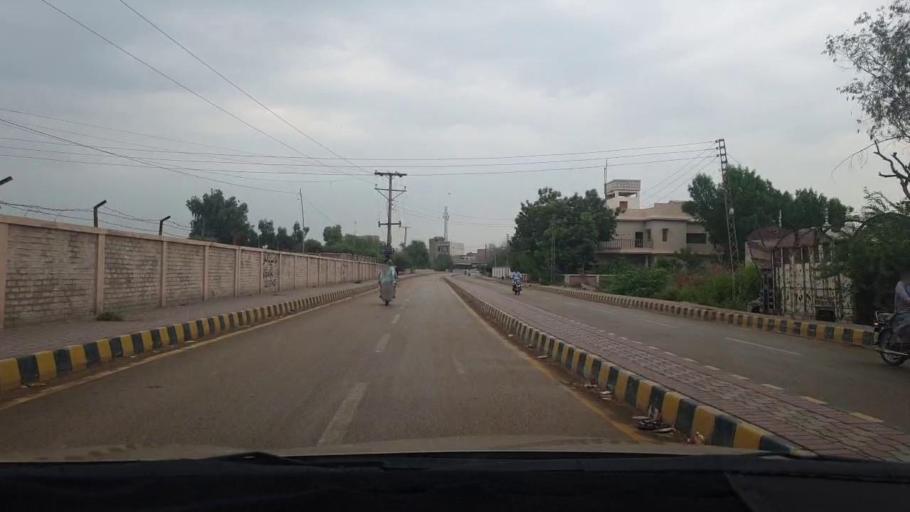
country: PK
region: Sindh
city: Larkana
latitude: 27.5643
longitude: 68.1974
